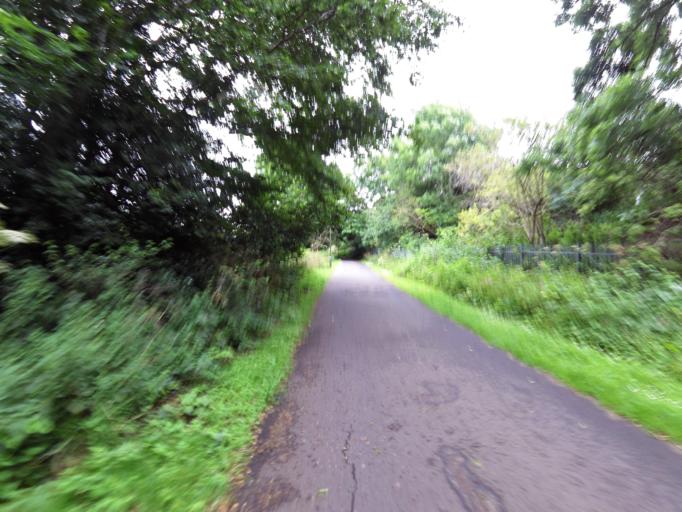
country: GB
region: Scotland
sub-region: West Lothian
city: Seafield
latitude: 55.9364
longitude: -3.1322
